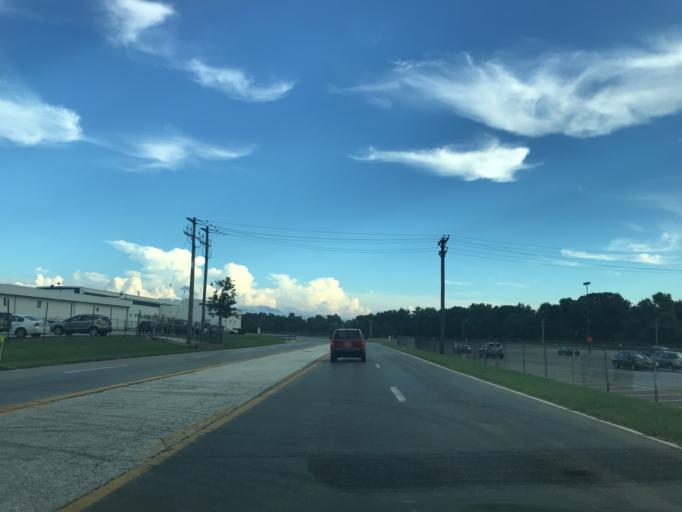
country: US
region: Maryland
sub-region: Baltimore County
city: Middle River
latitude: 39.3300
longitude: -76.4365
